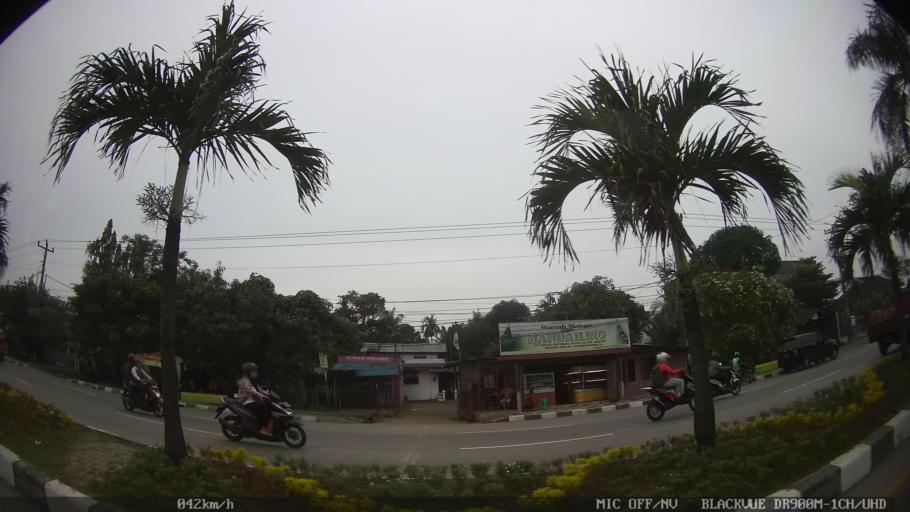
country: ID
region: North Sumatra
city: Deli Tua
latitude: 3.5377
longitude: 98.7060
